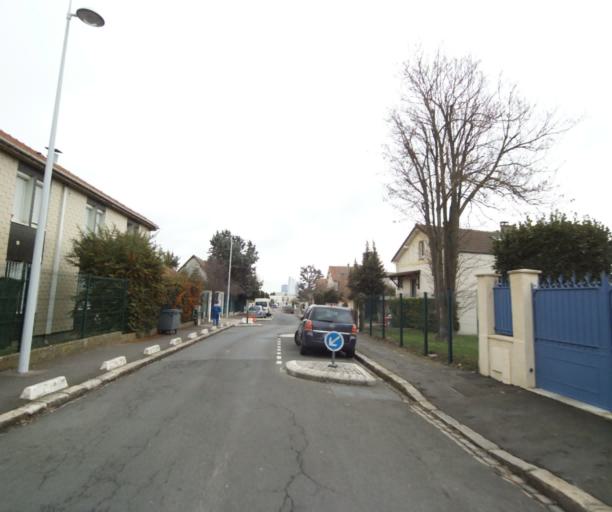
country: FR
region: Ile-de-France
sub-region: Departement des Hauts-de-Seine
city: Rueil-Malmaison
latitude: 48.8797
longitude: 2.2008
